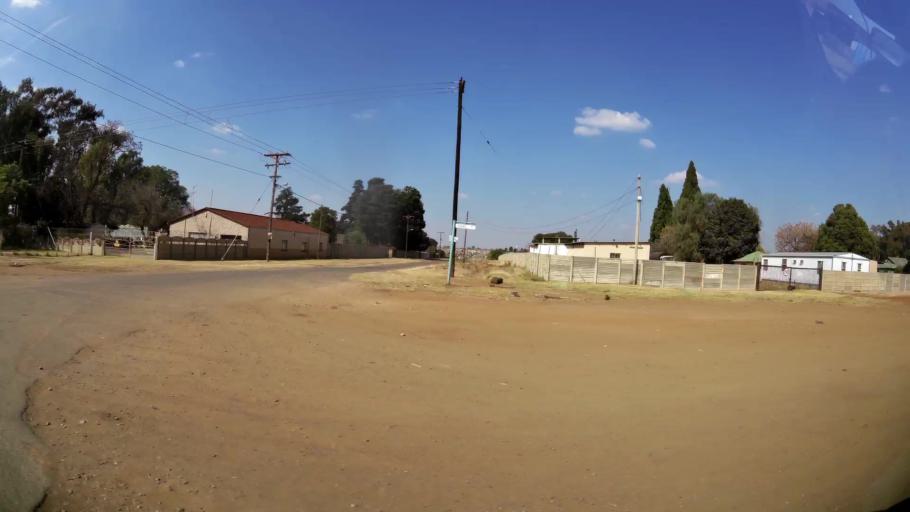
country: ZA
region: Gauteng
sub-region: Ekurhuleni Metropolitan Municipality
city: Benoni
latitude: -26.1174
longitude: 28.4059
